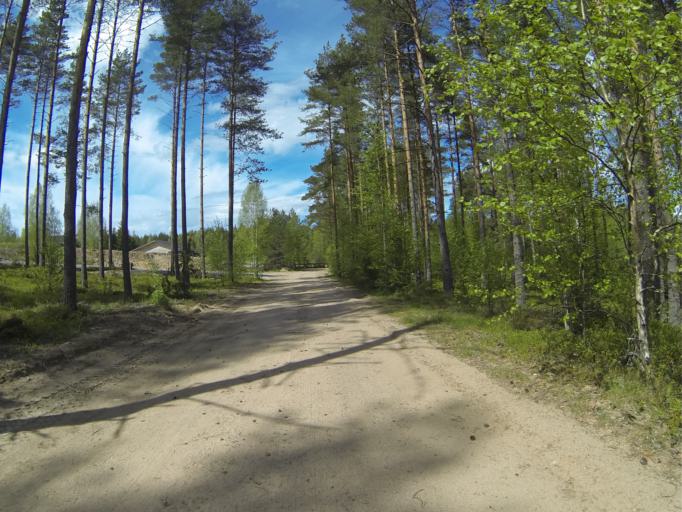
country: FI
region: Varsinais-Suomi
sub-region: Salo
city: Halikko
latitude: 60.3206
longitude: 23.0763
